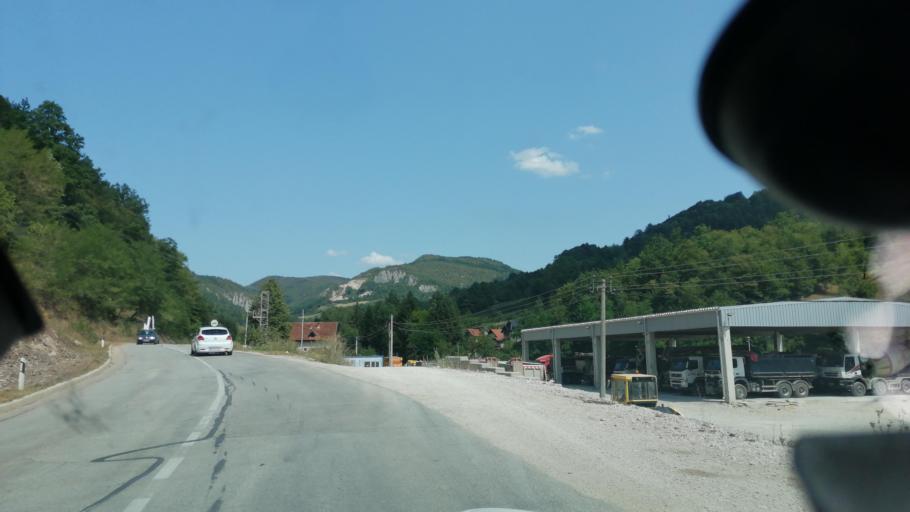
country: RS
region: Central Serbia
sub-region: Moravicki Okrug
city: Ivanjica
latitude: 43.6067
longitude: 20.2345
